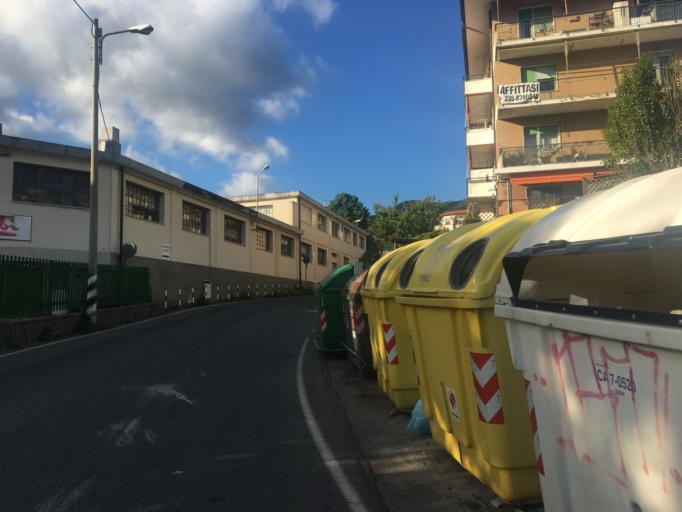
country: IT
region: Liguria
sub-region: Provincia di Genova
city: Piccarello
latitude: 44.4582
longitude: 8.9823
